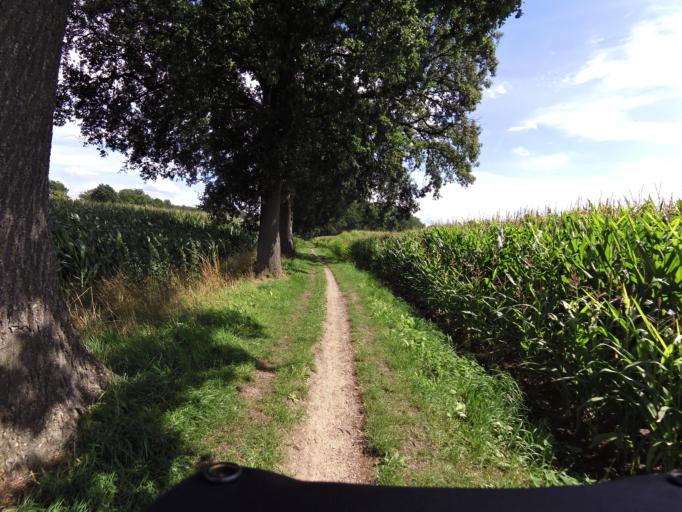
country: BE
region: Flanders
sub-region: Provincie Antwerpen
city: Hoogstraten
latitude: 51.4075
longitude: 4.7746
